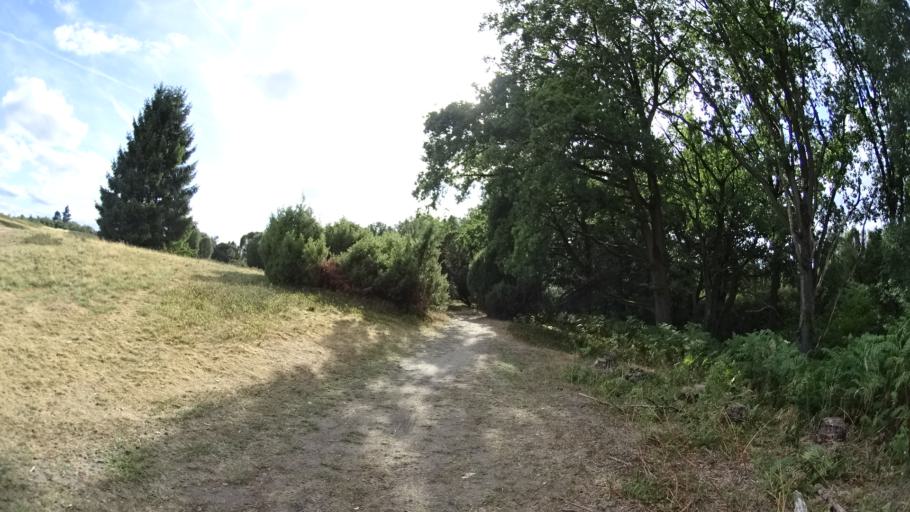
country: DE
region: Lower Saxony
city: Undeloh
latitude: 53.1561
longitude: 9.9268
